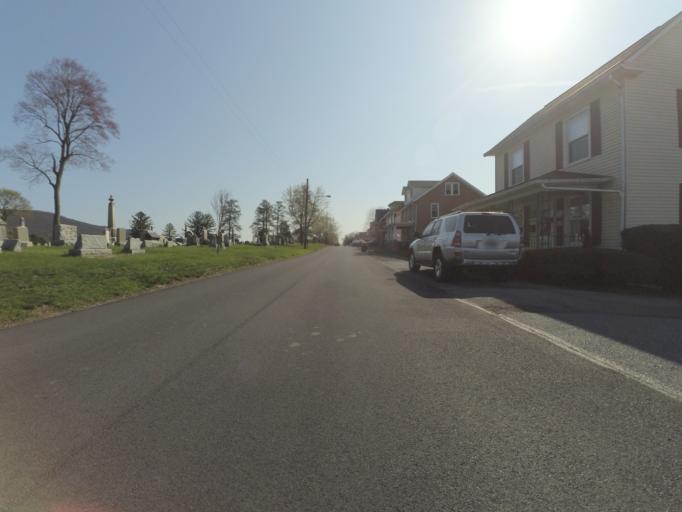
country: US
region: Pennsylvania
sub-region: Centre County
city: Bellefonte
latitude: 40.9129
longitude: -77.7737
